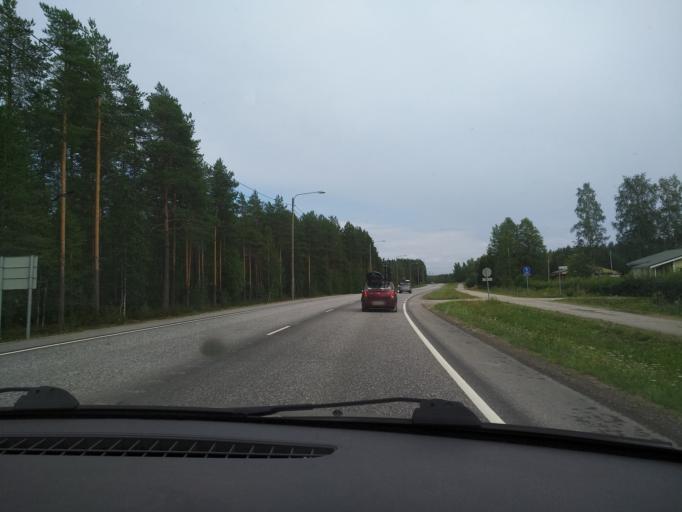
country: FI
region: Kainuu
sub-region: Kajaani
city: Paltamo
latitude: 64.4040
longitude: 27.8625
